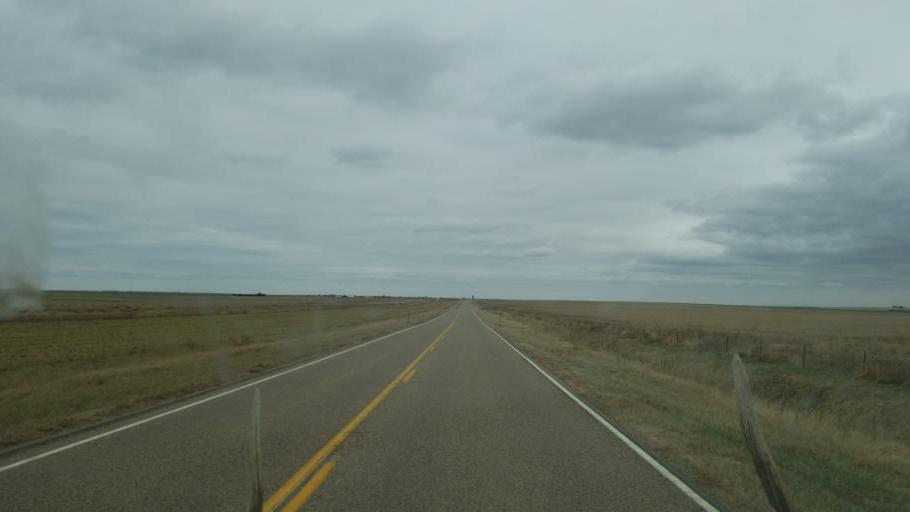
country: US
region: Colorado
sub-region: Cheyenne County
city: Cheyenne Wells
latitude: 38.8532
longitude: -102.2175
